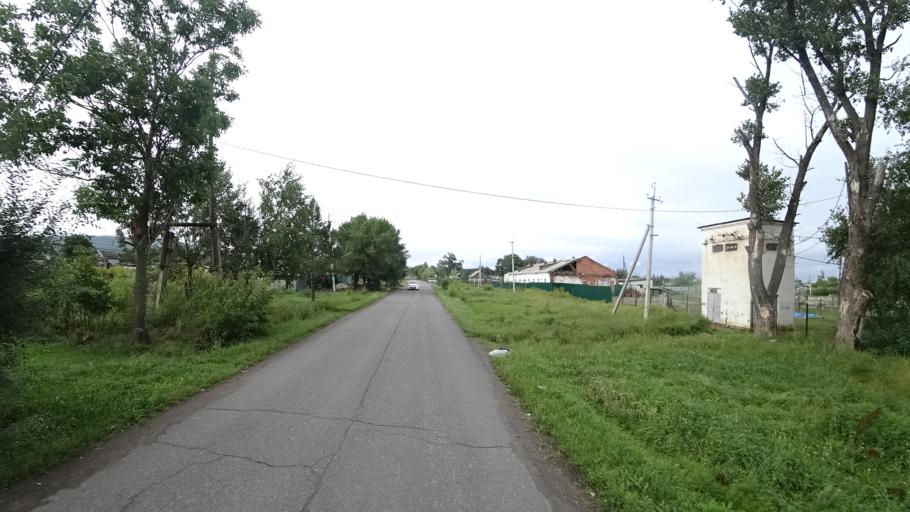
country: RU
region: Primorskiy
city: Chernigovka
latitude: 44.3369
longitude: 132.5792
